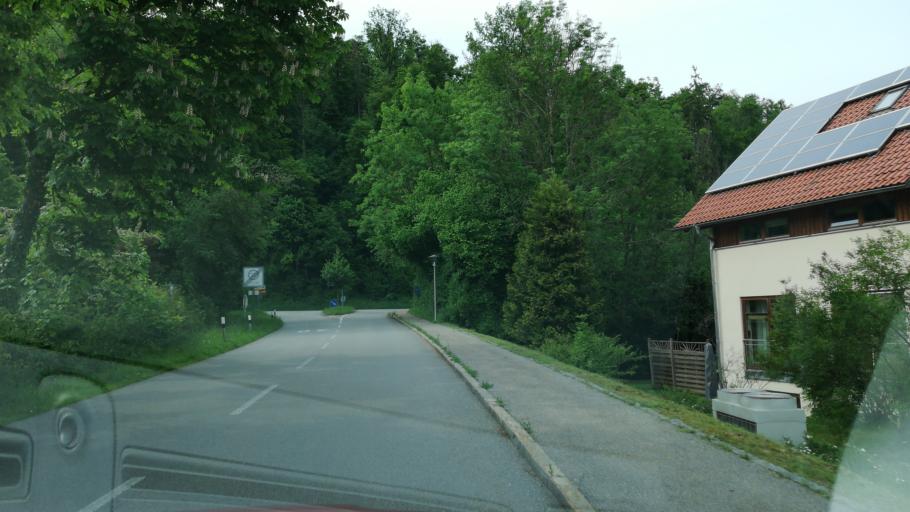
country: DE
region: Bavaria
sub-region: Upper Bavaria
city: Mehring
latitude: 48.1380
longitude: 12.7897
